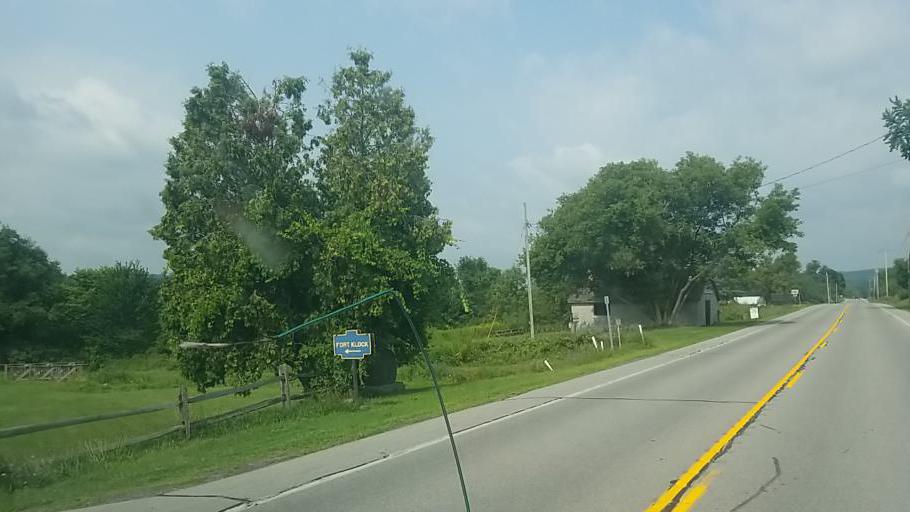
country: US
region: New York
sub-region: Montgomery County
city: Saint Johnsville
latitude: 42.9859
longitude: -74.6481
